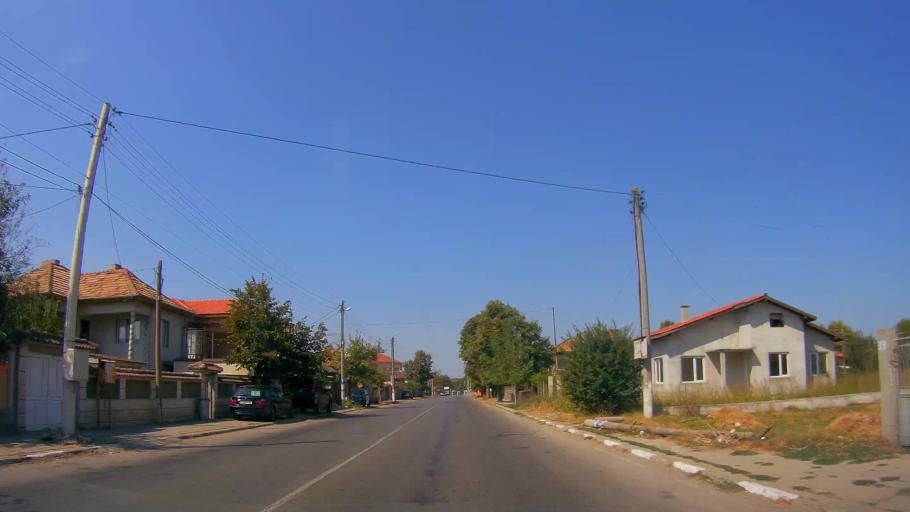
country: BG
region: Razgrad
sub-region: Obshtina Tsar Kaloyan
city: Tsar Kaloyan
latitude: 43.6049
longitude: 26.2415
